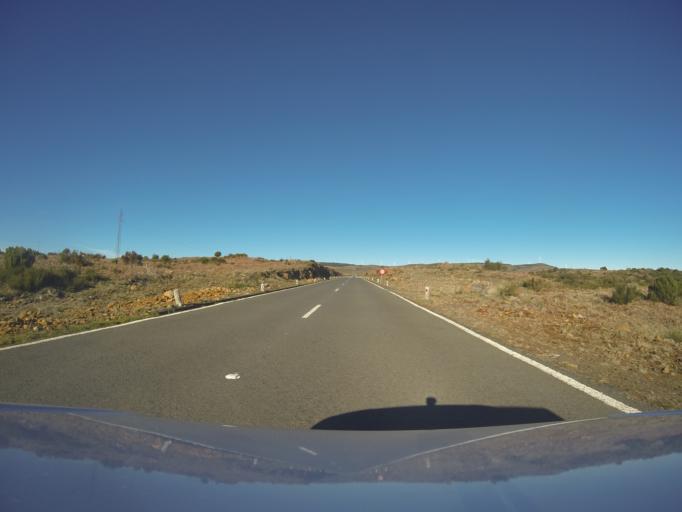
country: PT
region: Madeira
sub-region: Calheta
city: Arco da Calheta
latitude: 32.7548
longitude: -17.1039
